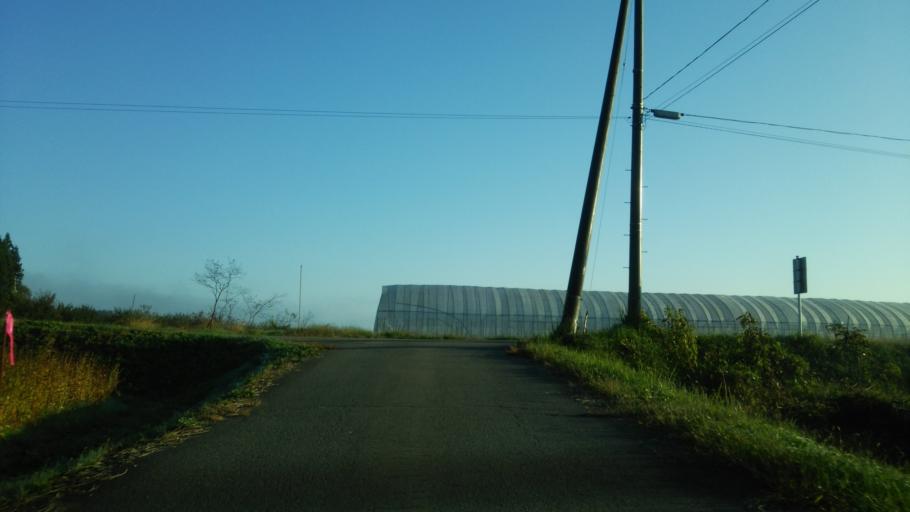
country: JP
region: Fukushima
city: Kitakata
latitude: 37.4333
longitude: 139.7996
